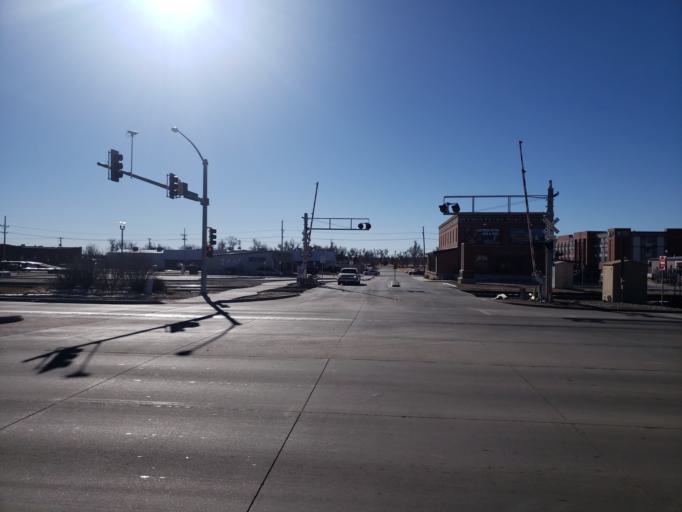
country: US
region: Kansas
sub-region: Ford County
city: Dodge City
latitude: 37.7529
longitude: -100.0215
